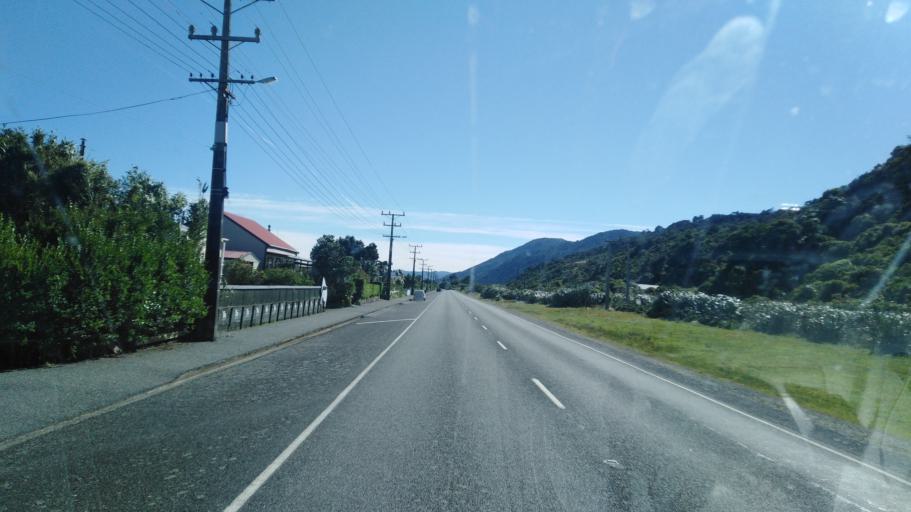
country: NZ
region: West Coast
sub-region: Buller District
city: Westport
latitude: -41.6246
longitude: 171.8585
